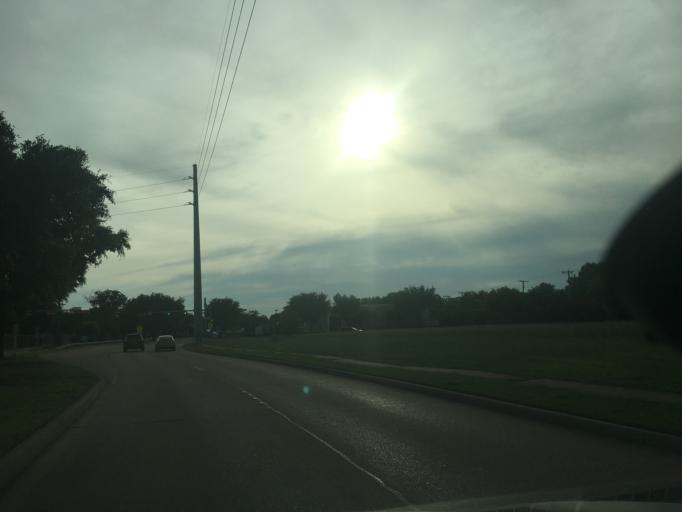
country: US
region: Texas
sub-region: Dallas County
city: Richardson
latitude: 32.9608
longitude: -96.6728
